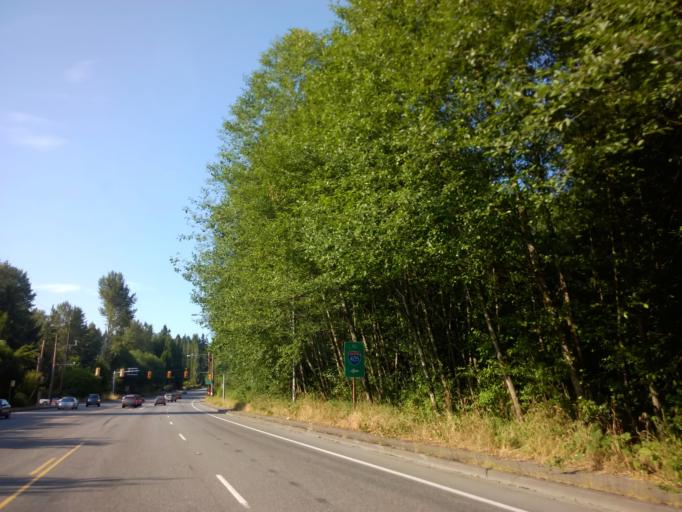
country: US
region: Washington
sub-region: King County
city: Cottage Lake
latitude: 47.7151
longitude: -122.0886
